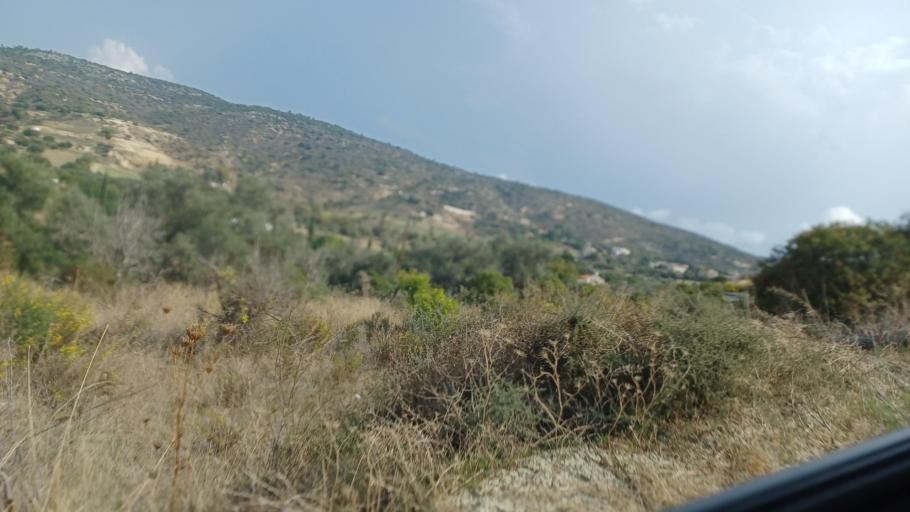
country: CY
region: Pafos
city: Polis
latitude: 35.0027
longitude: 32.4637
